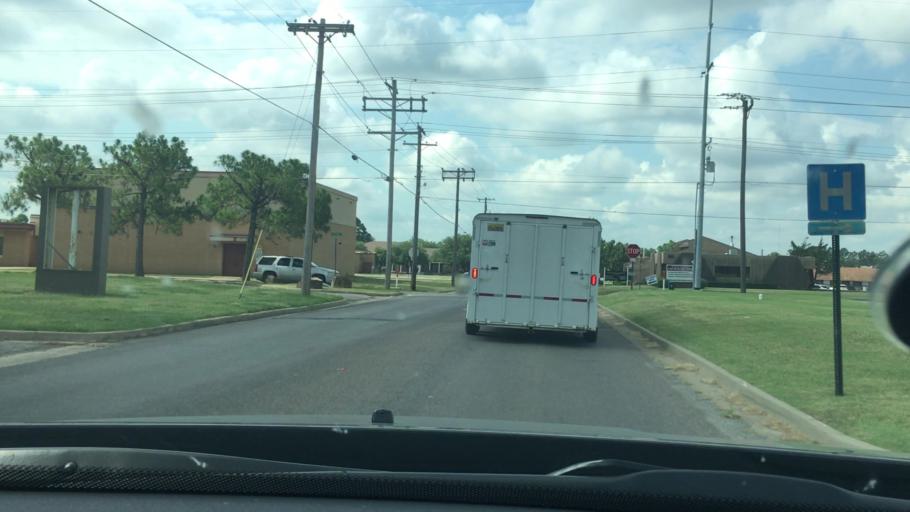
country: US
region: Oklahoma
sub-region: Bryan County
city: Durant
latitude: 34.0090
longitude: -96.3905
